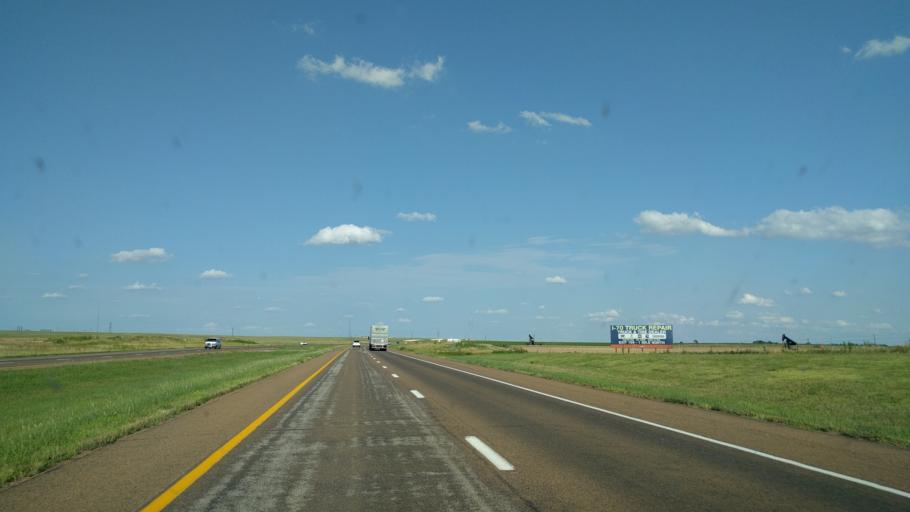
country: US
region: Kansas
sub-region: Ellis County
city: Hays
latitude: 38.9217
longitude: -99.3893
